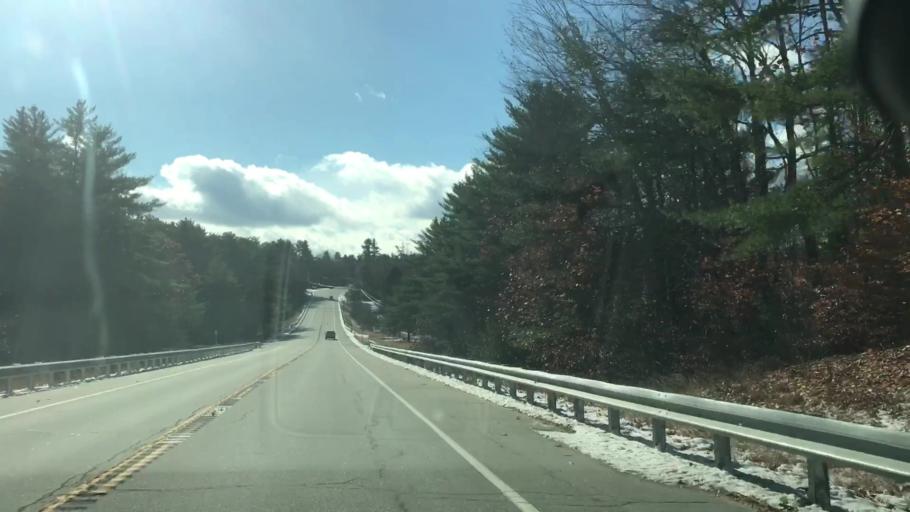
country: US
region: New Hampshire
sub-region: Carroll County
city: Ossipee
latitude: 43.6992
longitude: -71.1135
